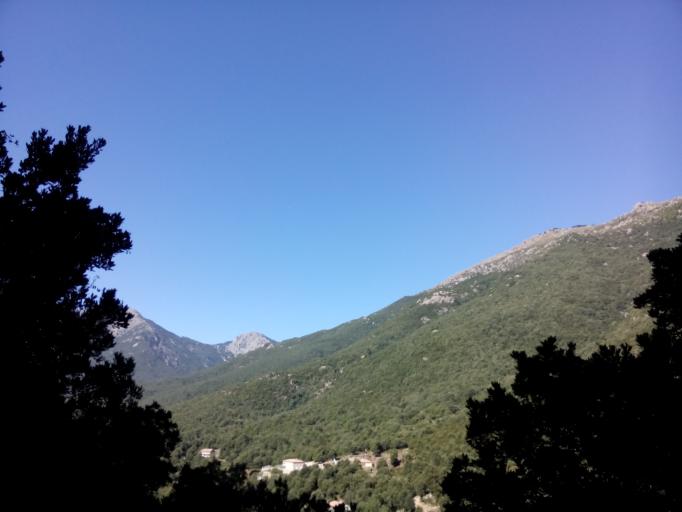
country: FR
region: Corsica
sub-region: Departement de la Haute-Corse
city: Ventiseri
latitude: 41.9291
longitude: 9.2695
